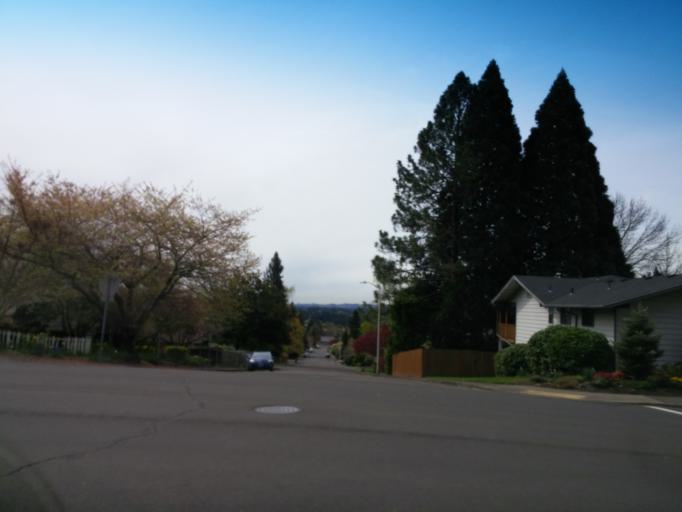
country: US
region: Oregon
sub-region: Washington County
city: Cedar Mill
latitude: 45.5311
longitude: -122.8023
